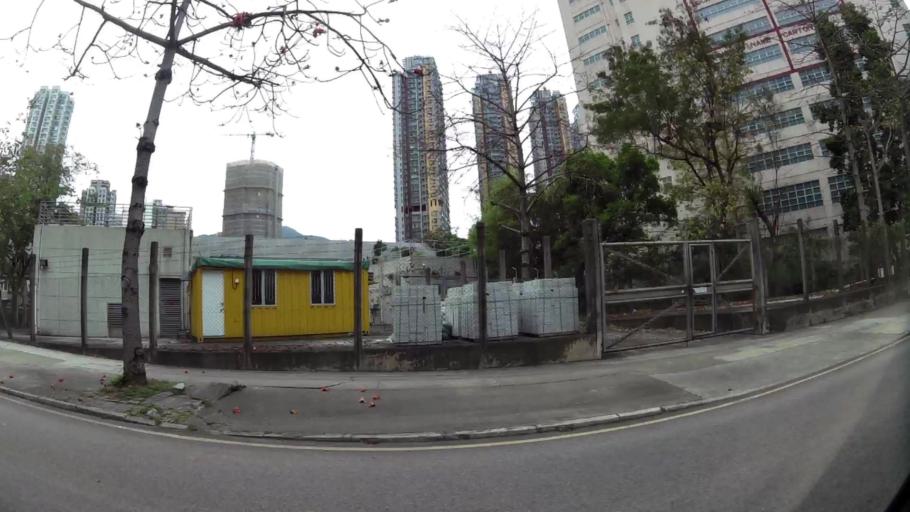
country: HK
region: Tuen Mun
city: Tuen Mun
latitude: 22.3983
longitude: 113.9728
